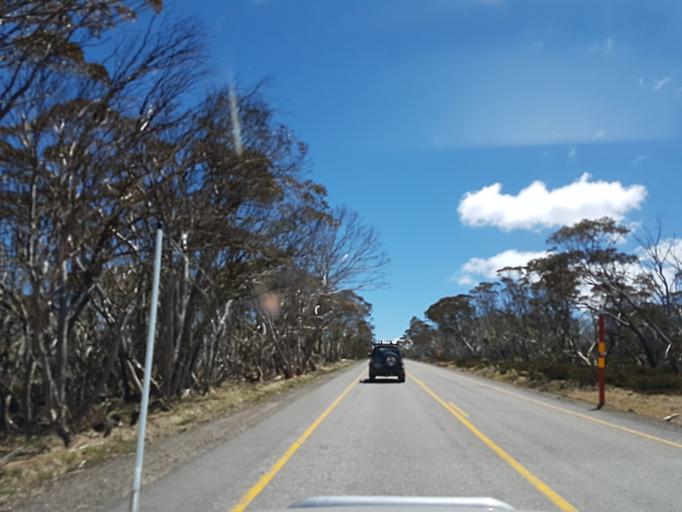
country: AU
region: Victoria
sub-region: Alpine
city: Mount Beauty
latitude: -37.0018
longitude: 147.1809
